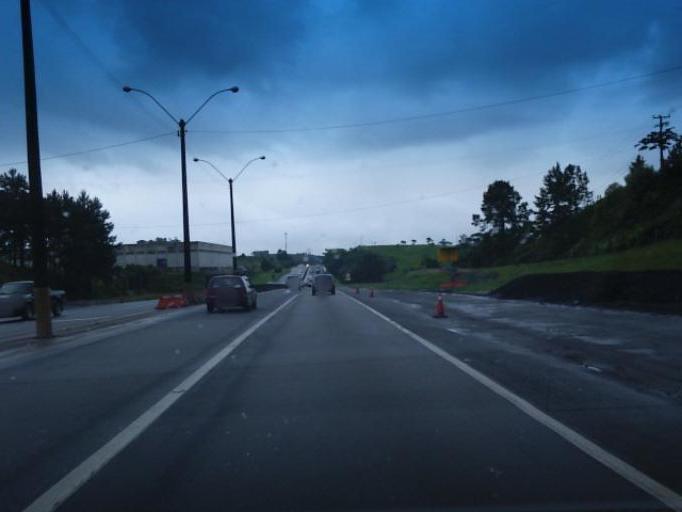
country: BR
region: Santa Catarina
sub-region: Barra Velha
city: Barra Velha
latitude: -26.6100
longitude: -48.7223
